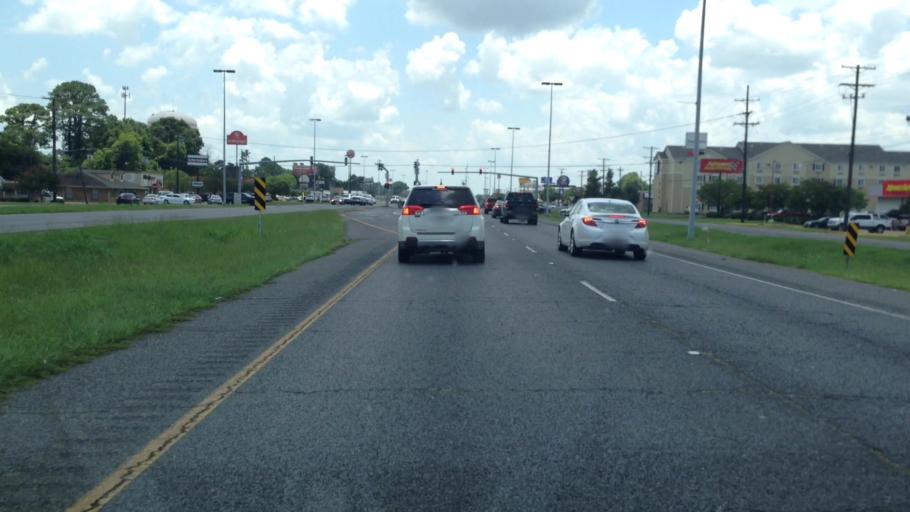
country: US
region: Louisiana
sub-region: Rapides Parish
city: Alexandria
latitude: 31.2942
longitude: -92.4781
